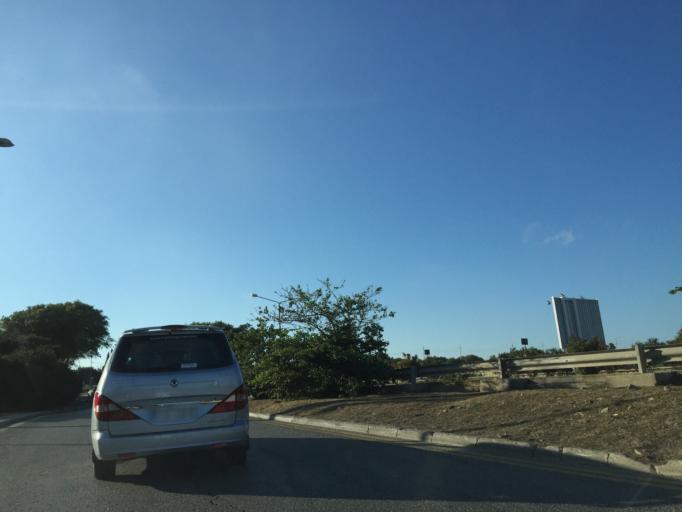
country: MT
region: Il-Gudja
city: Gudja
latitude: 35.8516
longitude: 14.4956
